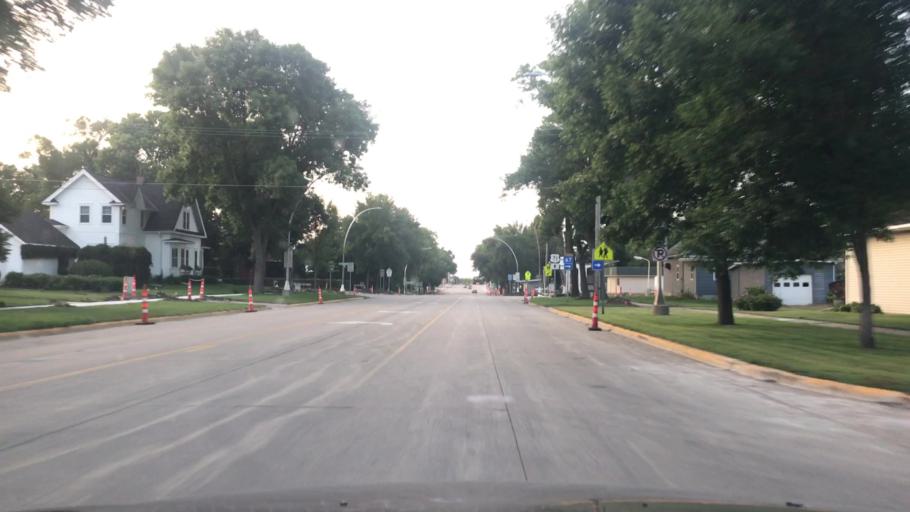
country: US
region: Minnesota
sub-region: Redwood County
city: Redwood Falls
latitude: 44.5342
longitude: -95.1195
